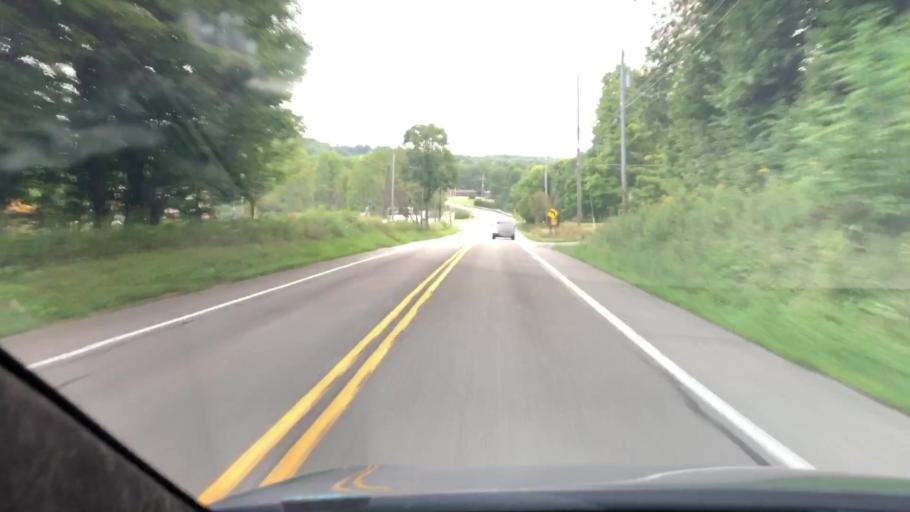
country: US
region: Pennsylvania
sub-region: Mercer County
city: Grove City
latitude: 41.1753
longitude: -79.9852
